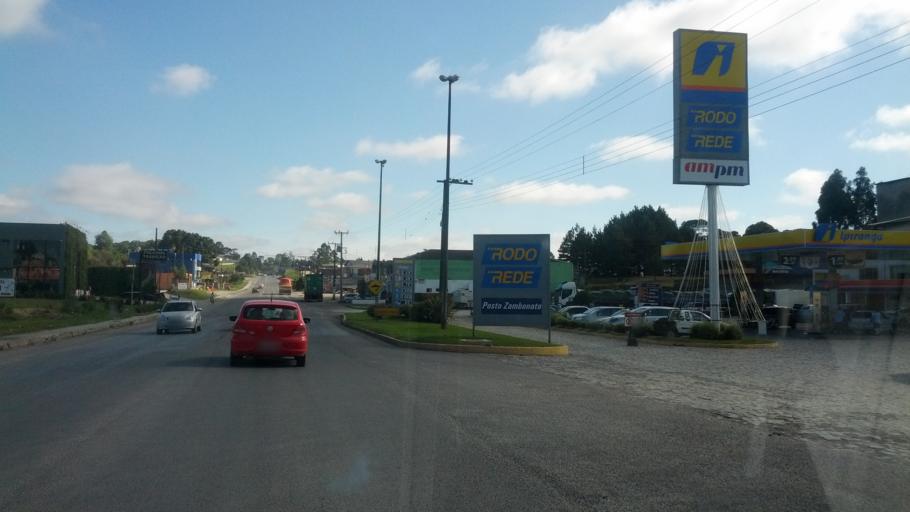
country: BR
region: Santa Catarina
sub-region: Otacilio Costa
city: Otacilio Costa
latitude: -27.4940
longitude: -50.1206
